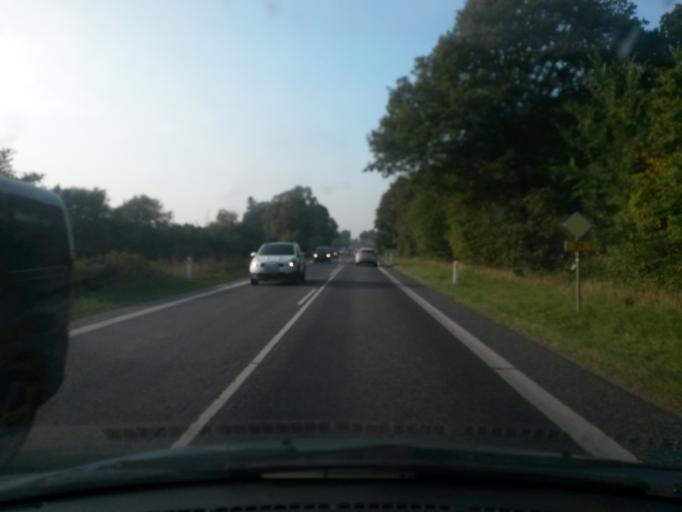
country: DK
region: Central Jutland
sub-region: Randers Kommune
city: Assentoft
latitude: 56.4076
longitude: 10.2340
